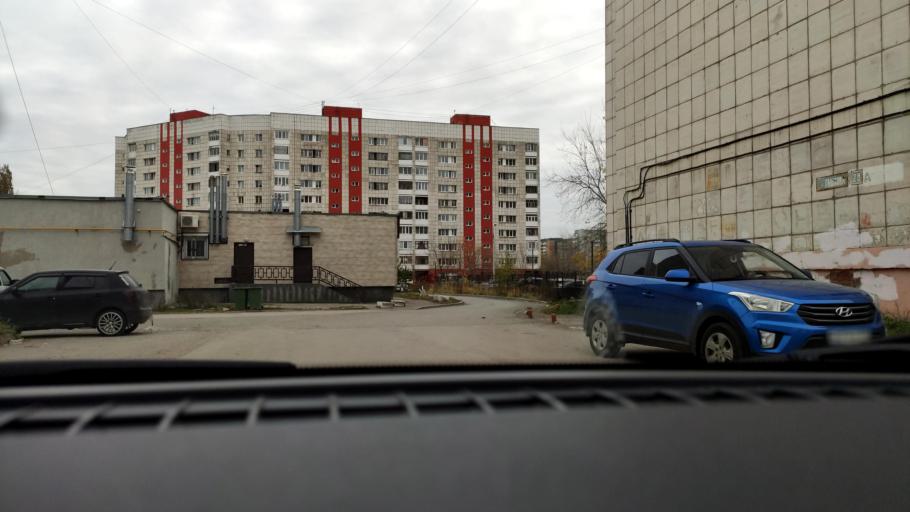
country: RU
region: Perm
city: Perm
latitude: 58.0588
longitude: 56.3457
